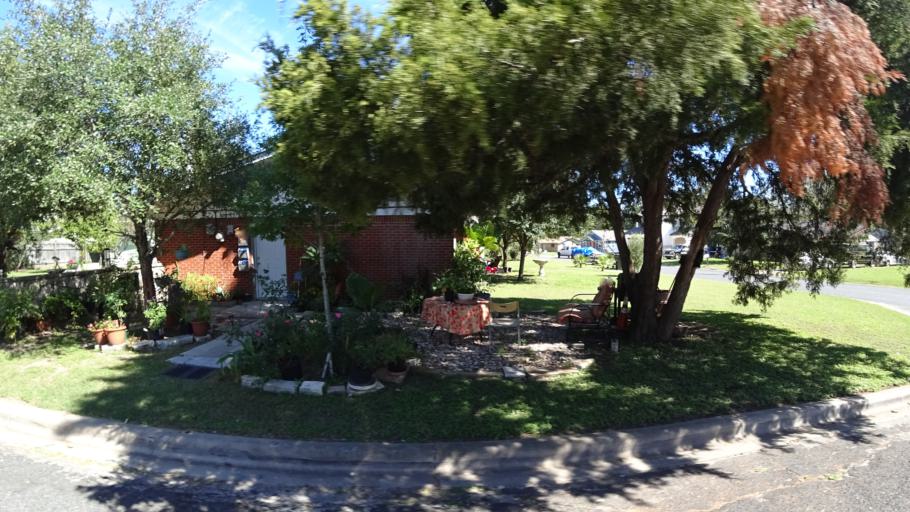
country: US
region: Texas
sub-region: Travis County
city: Austin
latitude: 30.1920
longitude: -97.7021
